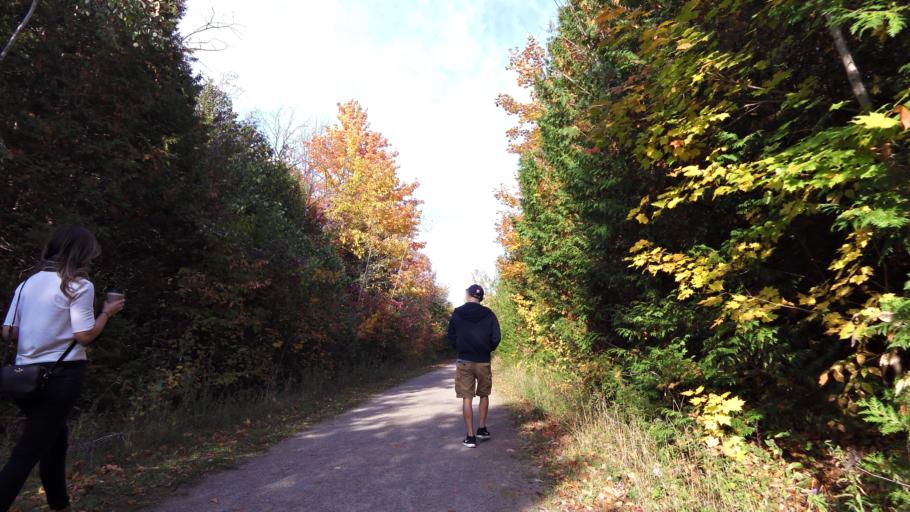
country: CA
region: Ontario
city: Orangeville
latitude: 43.8143
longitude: -80.0279
